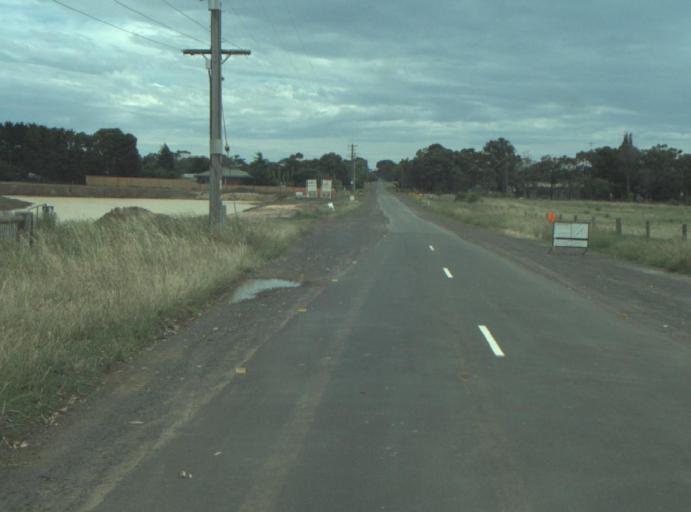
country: AU
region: Victoria
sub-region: Greater Geelong
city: Leopold
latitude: -38.2013
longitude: 144.4526
